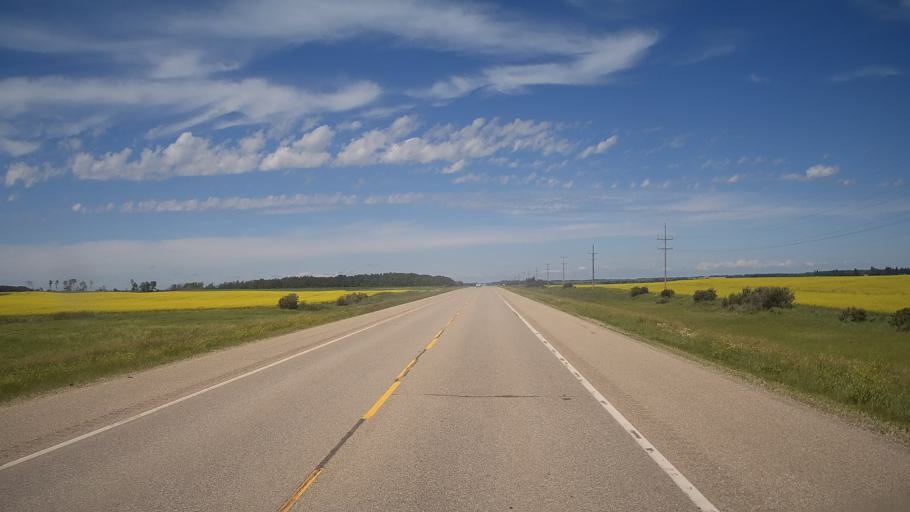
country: CA
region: Saskatchewan
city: Langenburg
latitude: 50.6701
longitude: -101.2761
